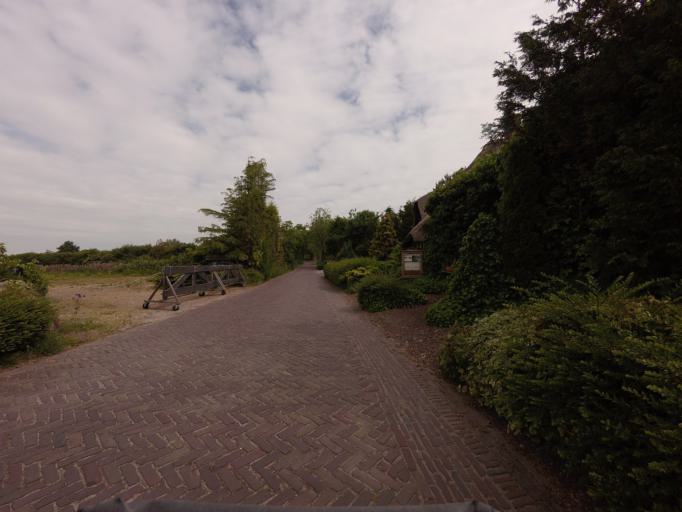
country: NL
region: North Holland
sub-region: Gemeente Medemblik
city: Opperdoes
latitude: 52.7103
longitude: 5.1073
